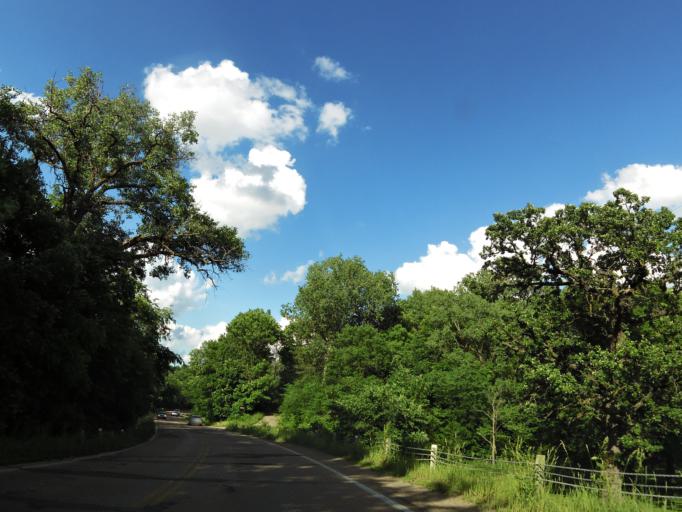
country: US
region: Minnesota
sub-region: Carver County
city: Chaska
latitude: 44.8006
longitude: -93.6255
